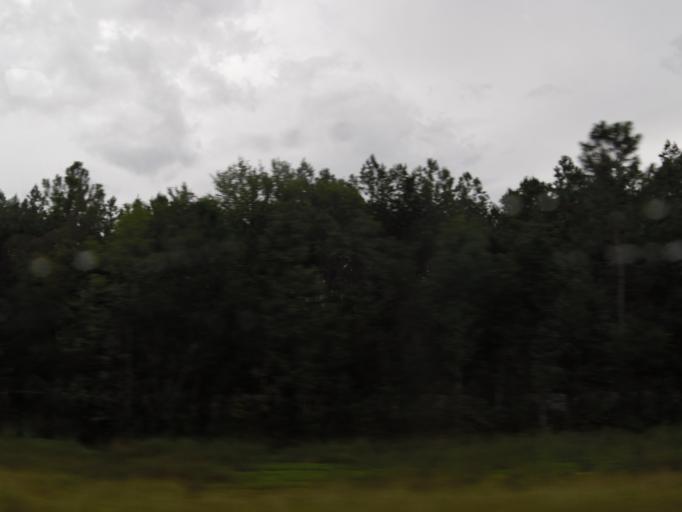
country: US
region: Georgia
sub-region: Wayne County
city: Jesup
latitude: 31.4543
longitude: -81.7021
